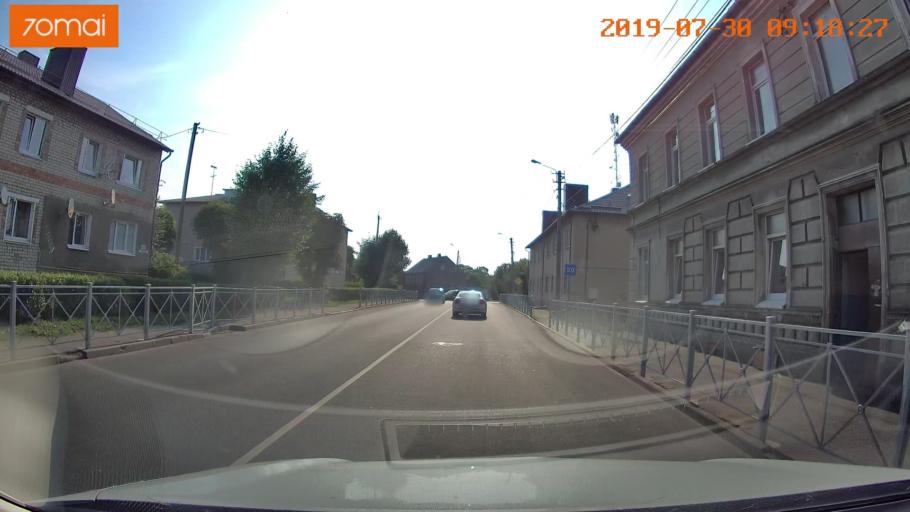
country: RU
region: Kaliningrad
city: Nesterov
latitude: 54.6307
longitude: 22.5762
